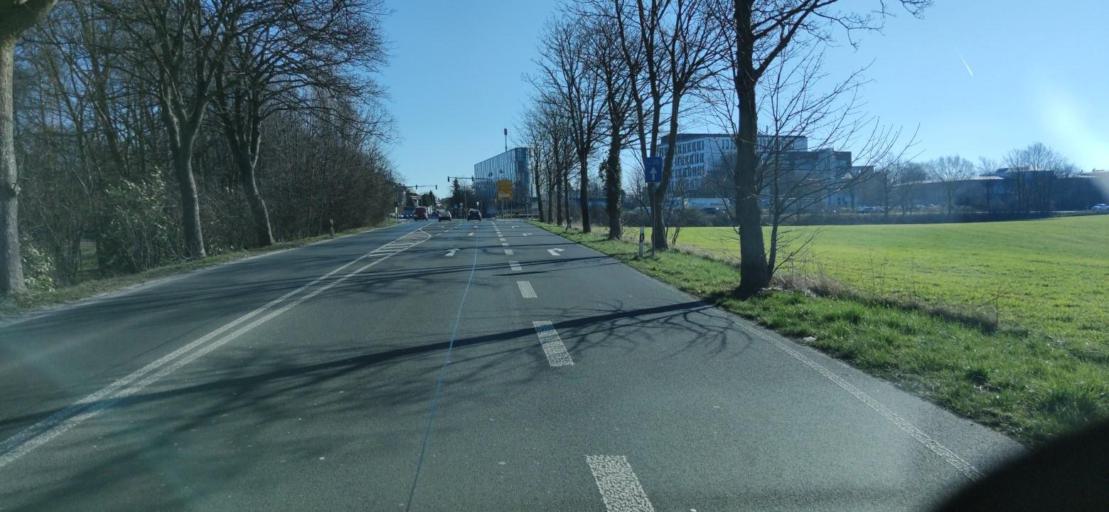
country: DE
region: North Rhine-Westphalia
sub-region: Regierungsbezirk Dusseldorf
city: Mettmann
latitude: 51.2558
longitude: 6.9475
